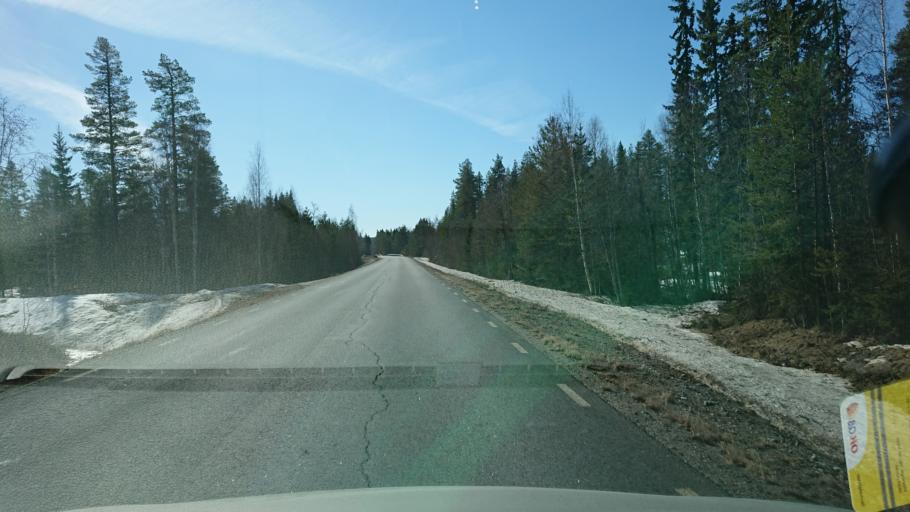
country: SE
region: Vaesterbotten
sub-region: Dorotea Kommun
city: Dorotea
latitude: 64.0885
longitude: 16.2603
